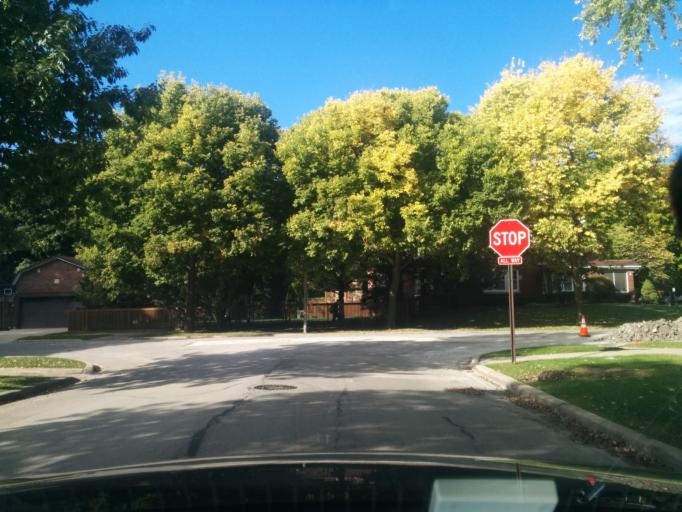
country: US
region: Illinois
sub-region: Cook County
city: River Forest
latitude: 41.8919
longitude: -87.8072
